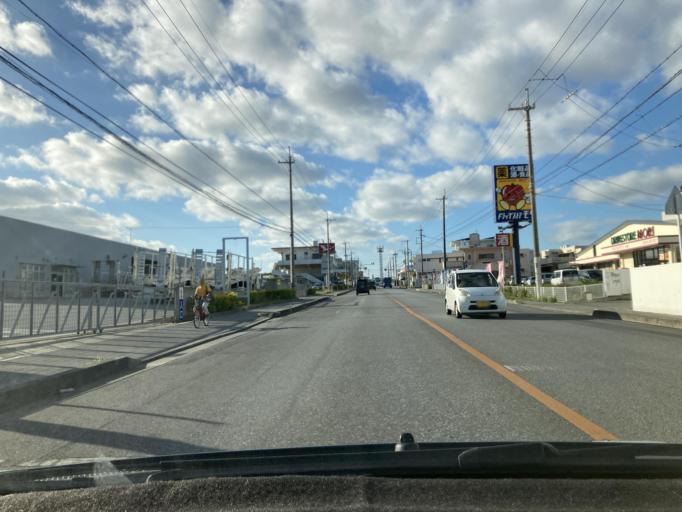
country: JP
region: Okinawa
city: Katsuren-haebaru
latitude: 26.3441
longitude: 127.8752
